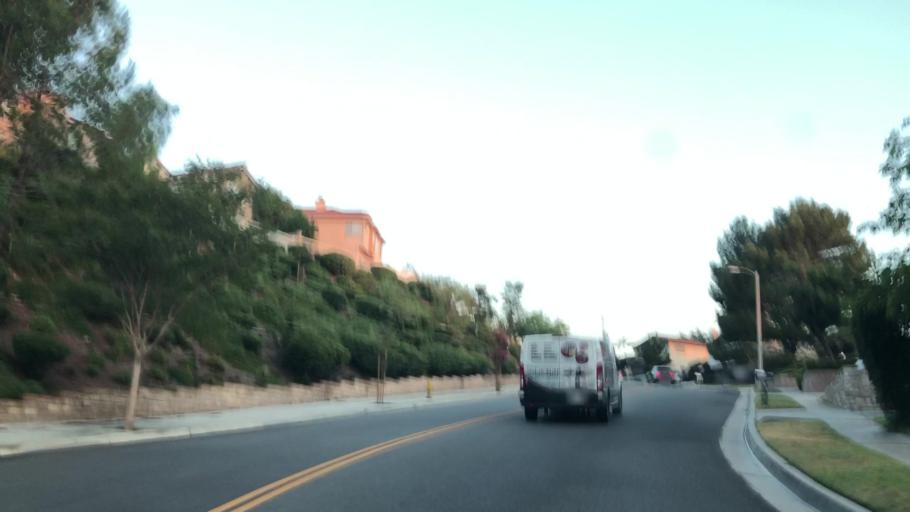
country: US
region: California
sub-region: Los Angeles County
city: Santa Clarita
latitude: 34.3952
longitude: -118.4731
